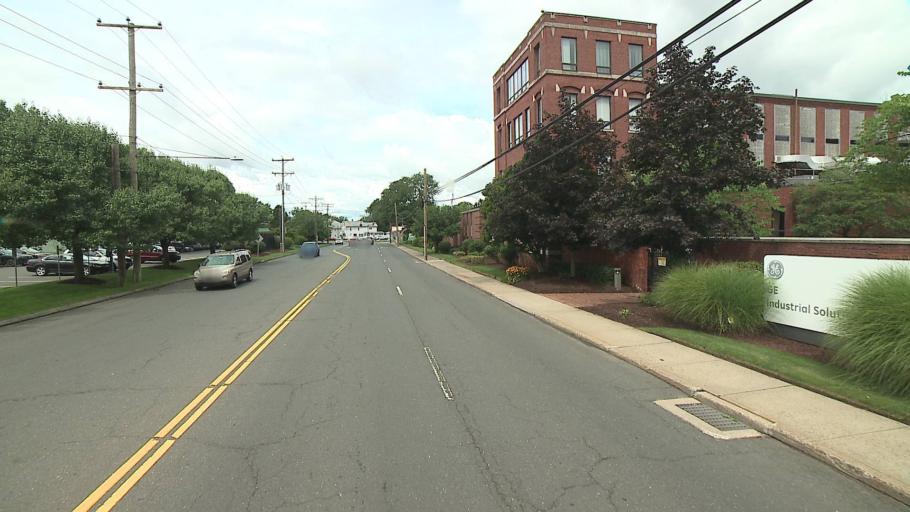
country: US
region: Connecticut
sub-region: Hartford County
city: Plainville
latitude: 41.6723
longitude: -72.8577
